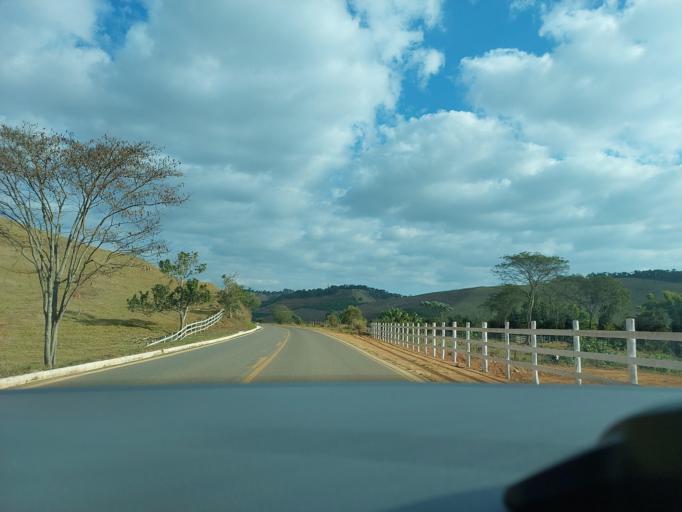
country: BR
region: Minas Gerais
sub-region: Visconde Do Rio Branco
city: Visconde do Rio Branco
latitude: -20.8624
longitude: -42.6703
